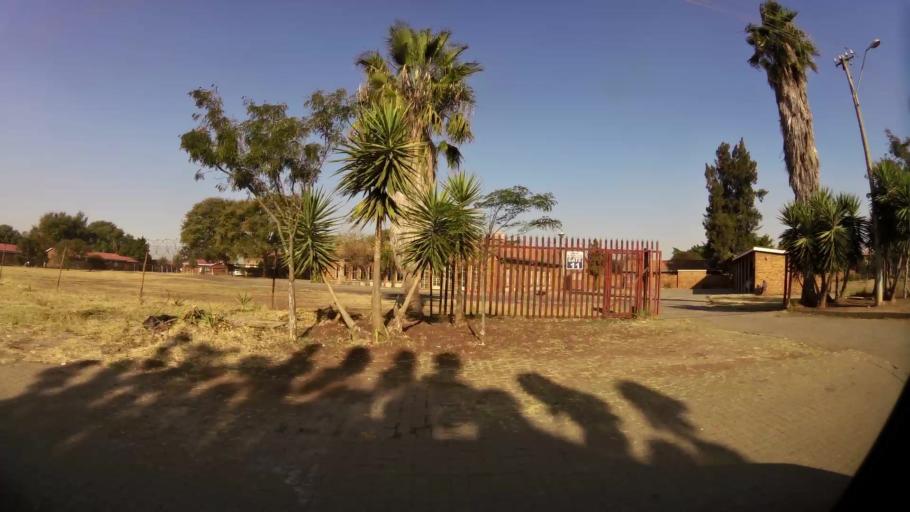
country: ZA
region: North-West
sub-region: Bojanala Platinum District Municipality
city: Rustenburg
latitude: -25.6455
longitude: 27.2394
